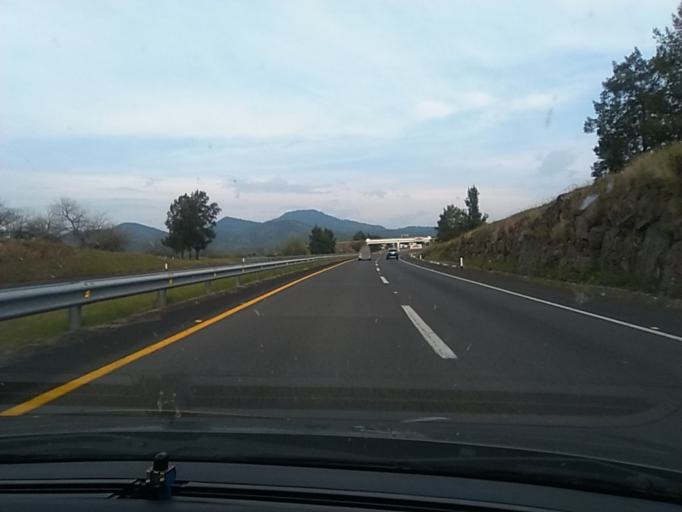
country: MX
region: Michoacan
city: Zinapecuaro
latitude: 19.9031
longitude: -100.7995
